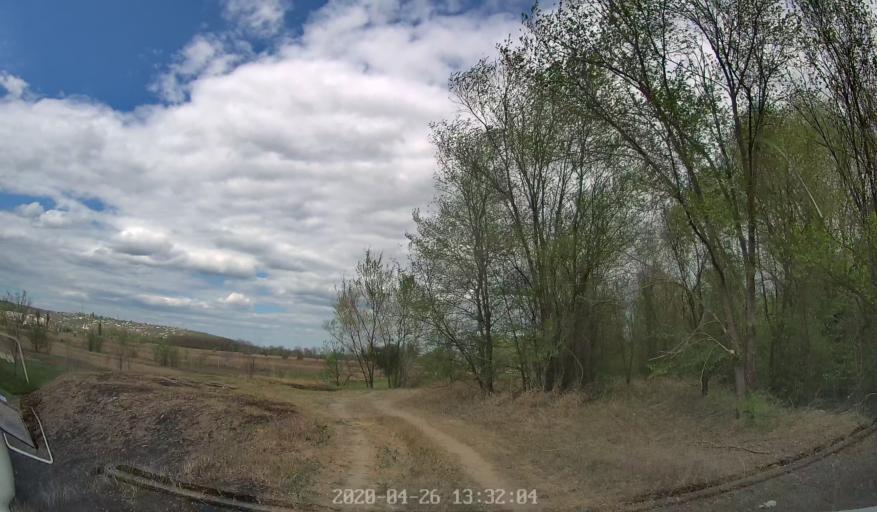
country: MD
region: Criuleni
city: Criuleni
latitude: 47.2084
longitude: 29.1777
